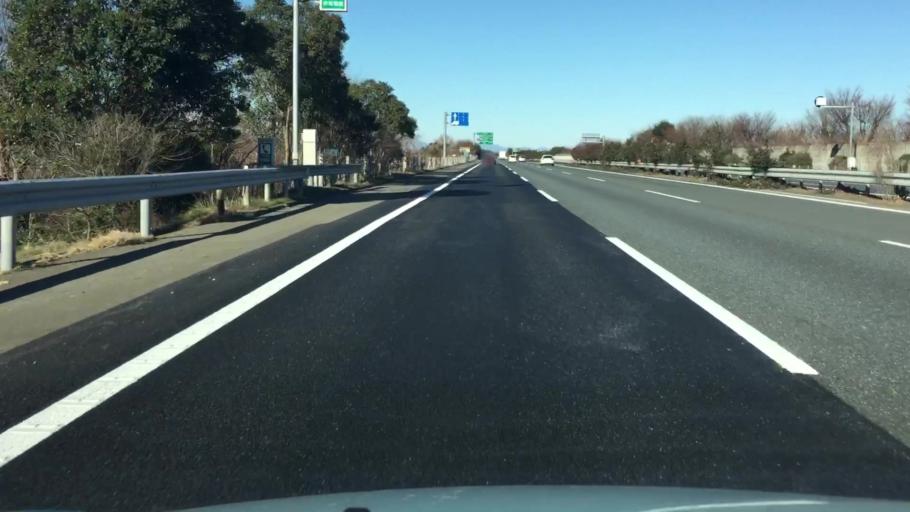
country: JP
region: Saitama
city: Yorii
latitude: 36.1296
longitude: 139.2391
